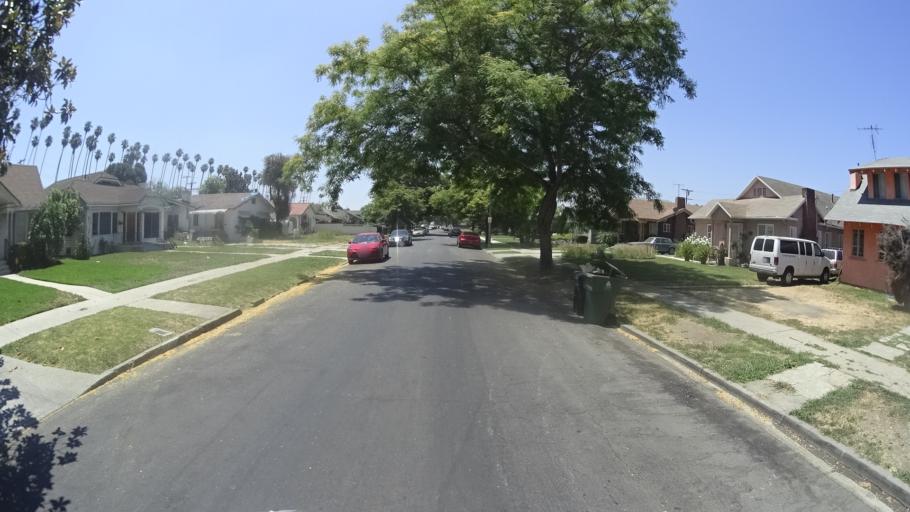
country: US
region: California
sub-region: Los Angeles County
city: View Park-Windsor Hills
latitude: 33.9992
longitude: -118.3214
